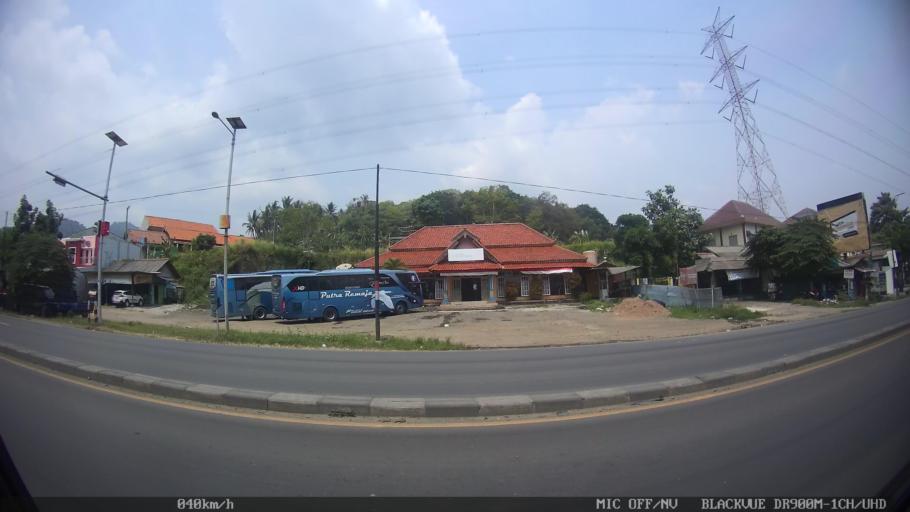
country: ID
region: Banten
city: Curug
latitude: -5.9635
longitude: 106.0062
